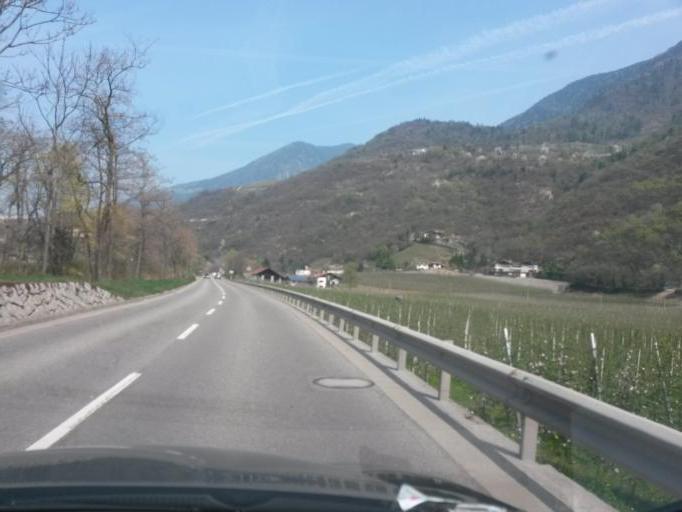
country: IT
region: Trentino-Alto Adige
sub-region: Bolzano
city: Sinigo
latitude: 46.6506
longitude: 11.1805
